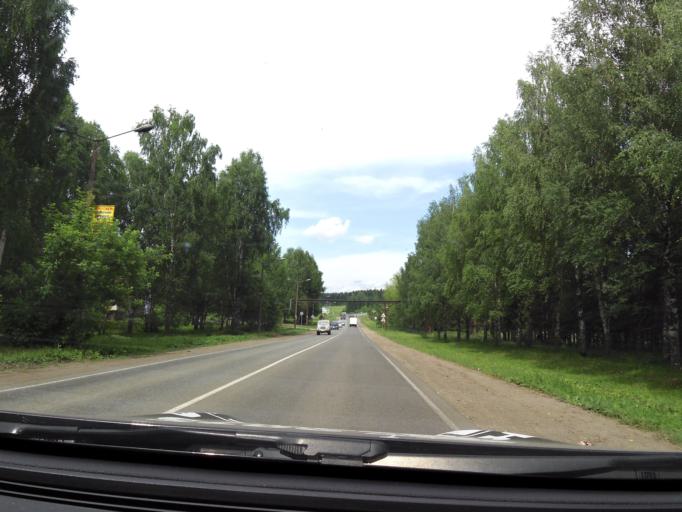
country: RU
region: Kirov
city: Vakhrushi
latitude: 58.6872
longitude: 50.0386
